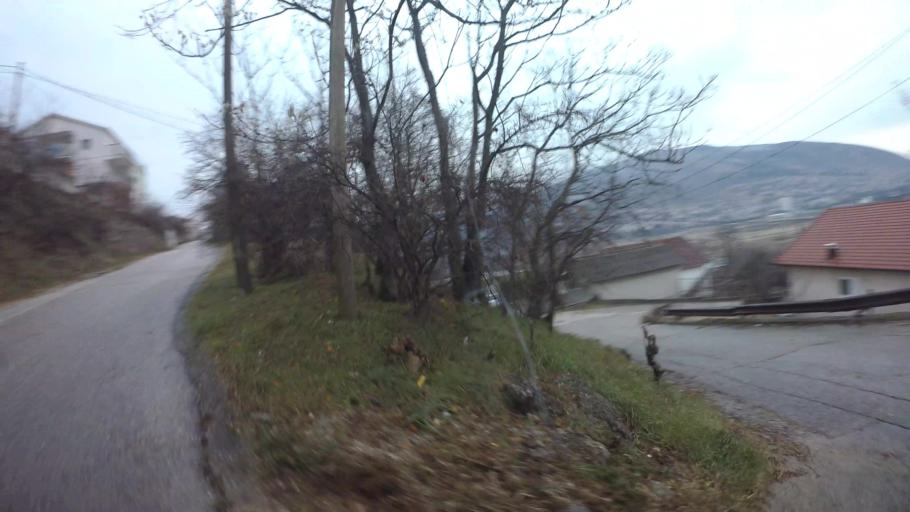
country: BA
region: Federation of Bosnia and Herzegovina
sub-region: Hercegovacko-Bosanski Kanton
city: Mostar
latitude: 43.3636
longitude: 17.8025
